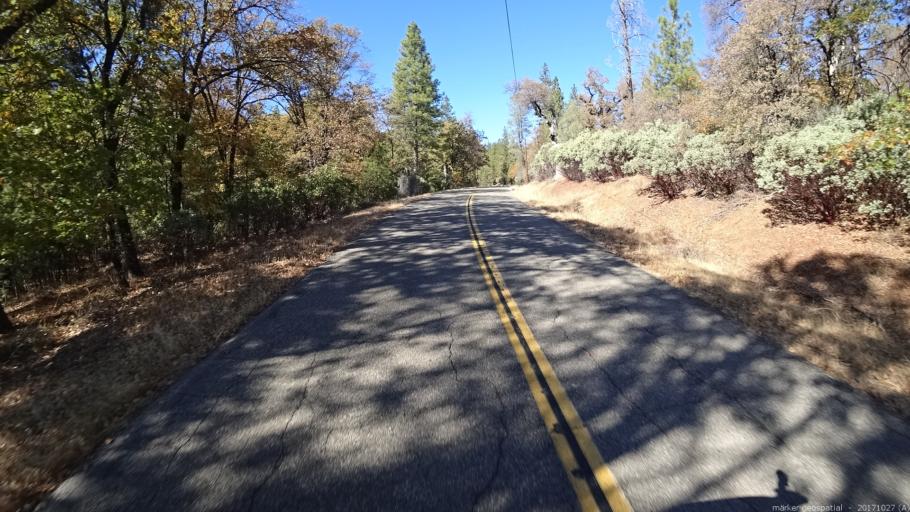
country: US
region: California
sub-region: Shasta County
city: Shingletown
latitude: 40.6825
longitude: -121.8886
